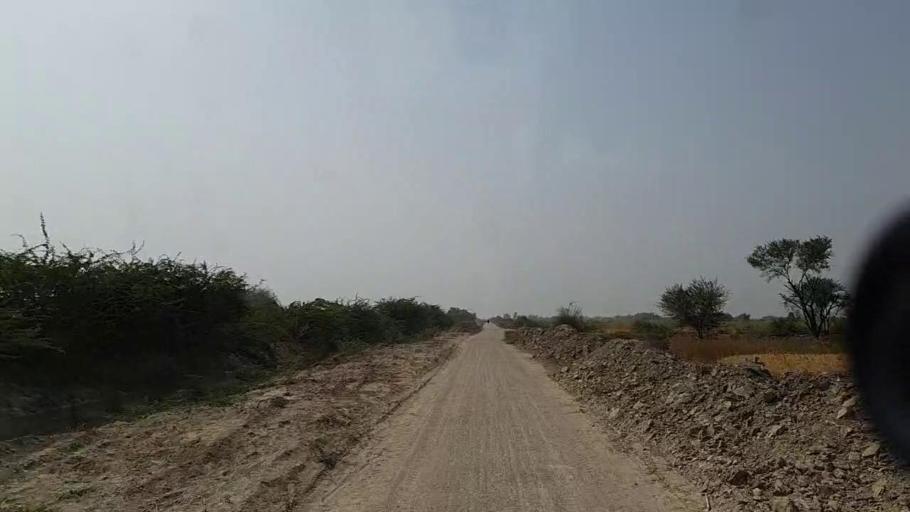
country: PK
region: Sindh
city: Naukot
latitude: 24.7713
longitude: 69.3242
